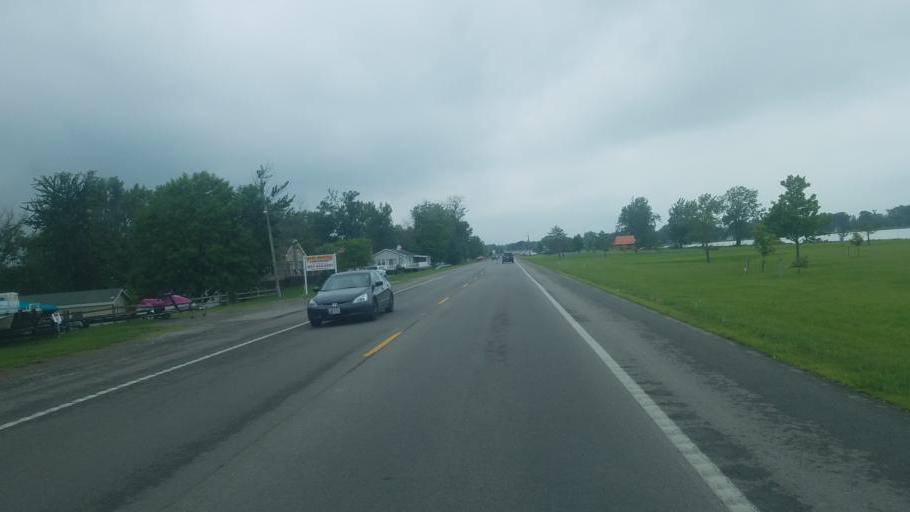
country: US
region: Ohio
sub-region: Logan County
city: Lakeview
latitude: 40.4828
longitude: -83.9140
